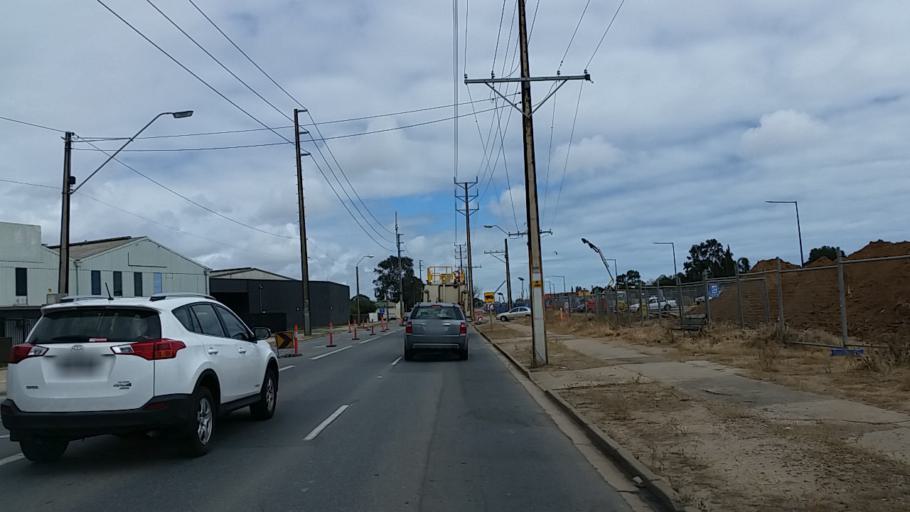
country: AU
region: South Australia
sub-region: Charles Sturt
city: Allenby Gardens
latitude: -34.8904
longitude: 138.5695
